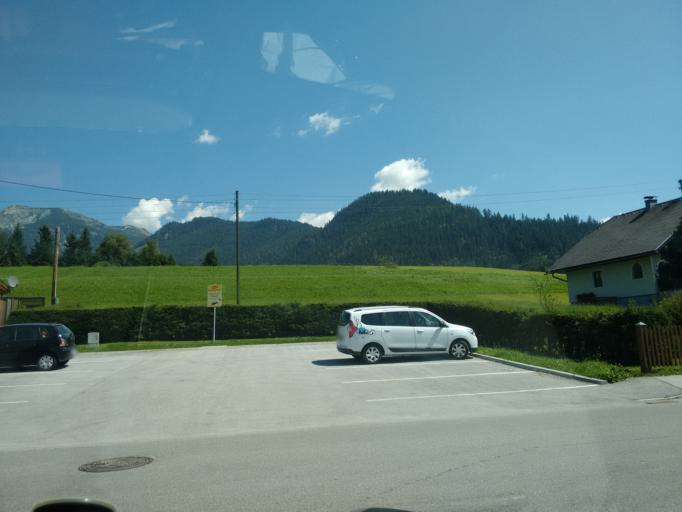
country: AT
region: Styria
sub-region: Politischer Bezirk Liezen
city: Tauplitz
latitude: 47.5578
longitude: 13.9244
